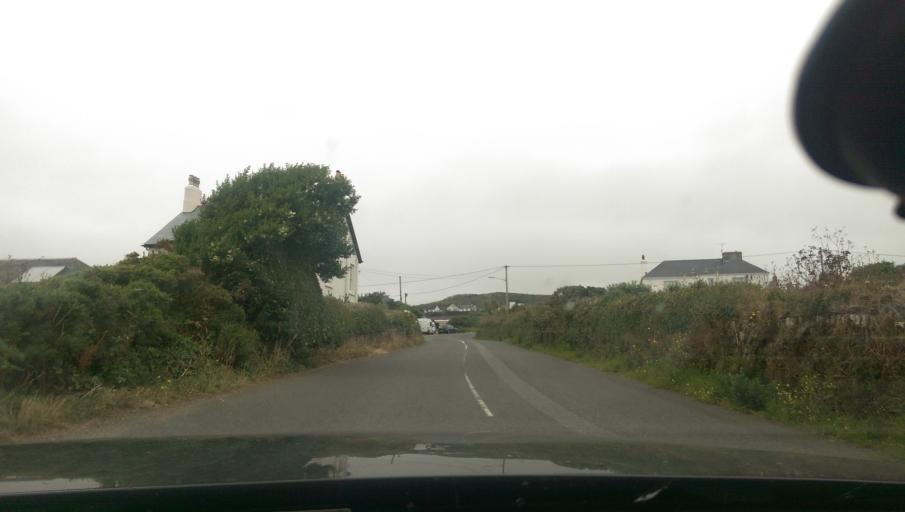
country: GB
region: England
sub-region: Cornwall
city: Saint Just
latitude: 50.1149
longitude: -5.6802
